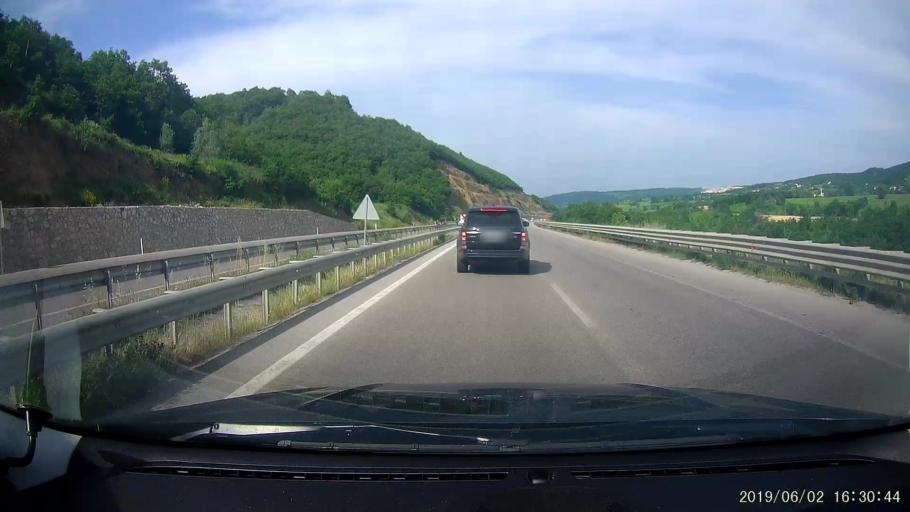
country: TR
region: Samsun
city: Ladik
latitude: 41.0279
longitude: 35.8884
